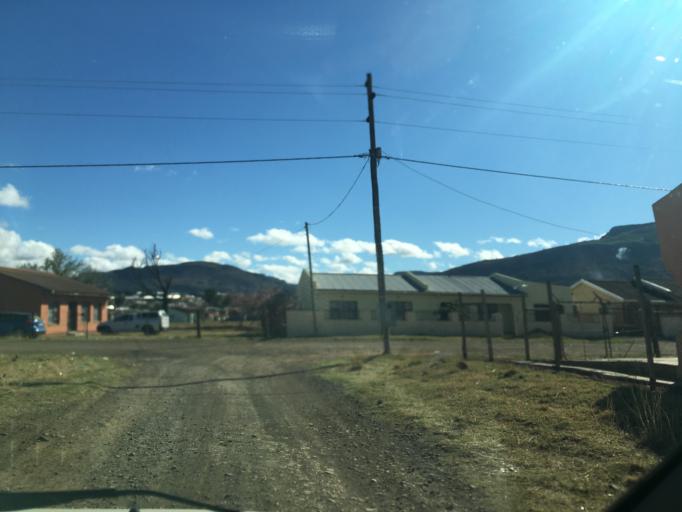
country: ZA
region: Eastern Cape
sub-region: Chris Hani District Municipality
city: Cala
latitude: -31.5346
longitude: 27.6928
